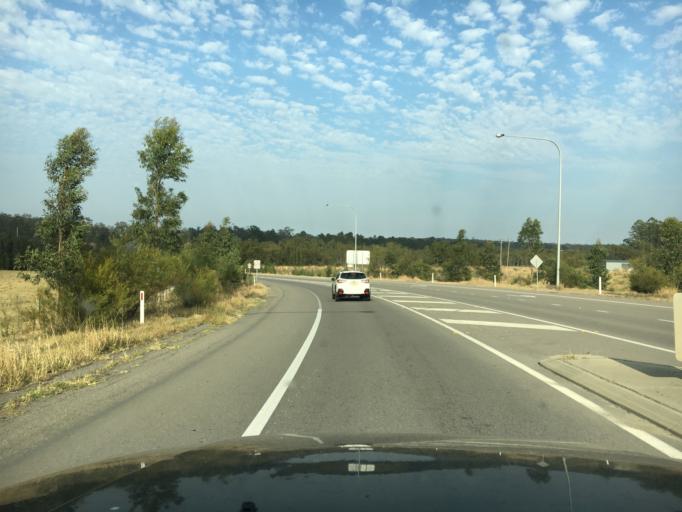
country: AU
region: New South Wales
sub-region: Cessnock
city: Branxton
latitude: -32.6632
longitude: 151.3687
